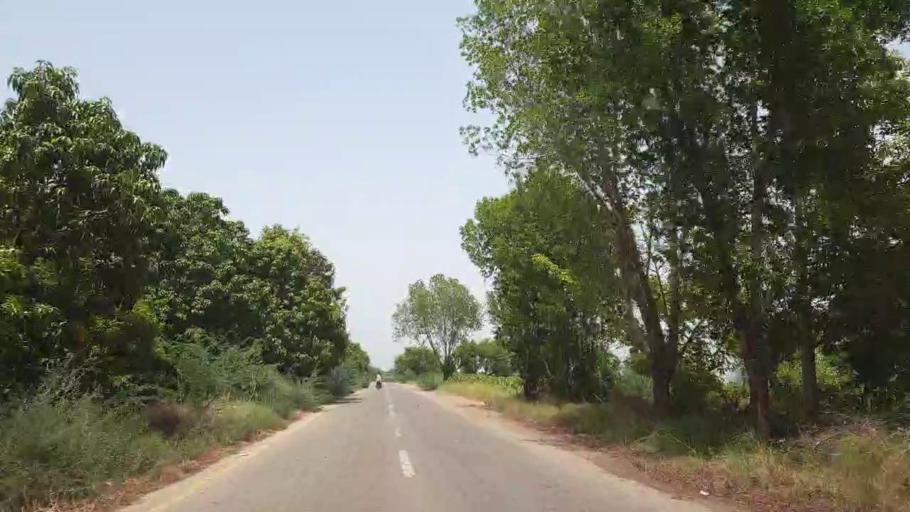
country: PK
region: Sindh
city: Sakrand
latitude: 26.1920
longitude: 68.2360
